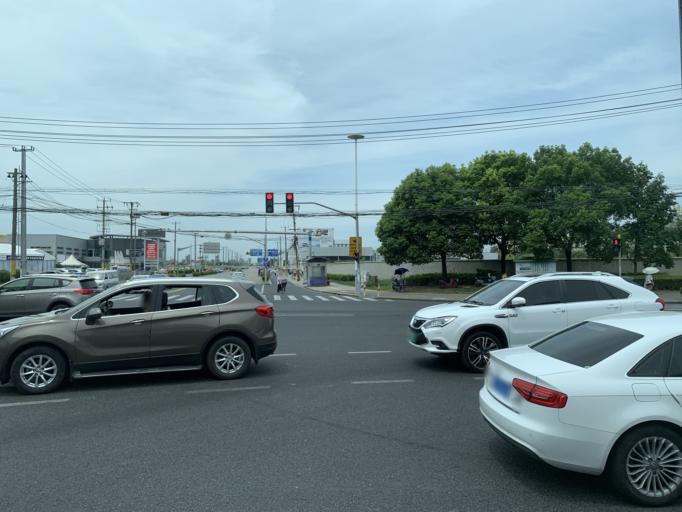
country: CN
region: Shanghai Shi
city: Kangqiao
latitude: 31.1590
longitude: 121.5600
